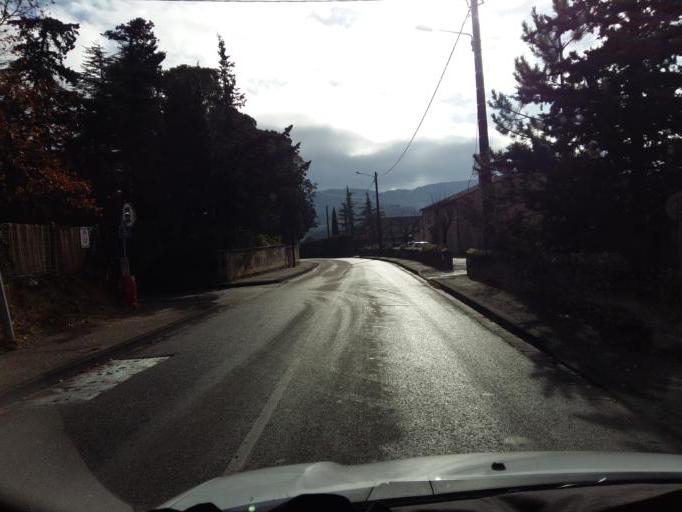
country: FR
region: Provence-Alpes-Cote d'Azur
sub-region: Departement du Vaucluse
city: Vaison-la-Romaine
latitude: 44.2460
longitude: 5.0688
